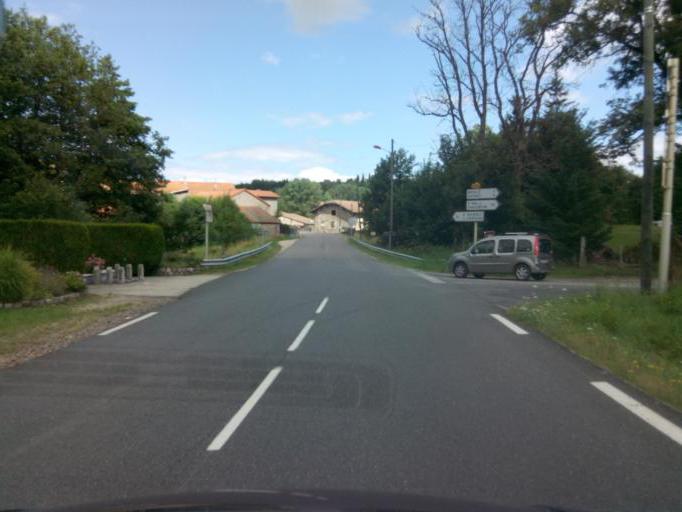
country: FR
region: Rhone-Alpes
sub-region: Departement de la Loire
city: Saint-Bonnet-le-Chateau
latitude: 45.4145
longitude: 4.0071
